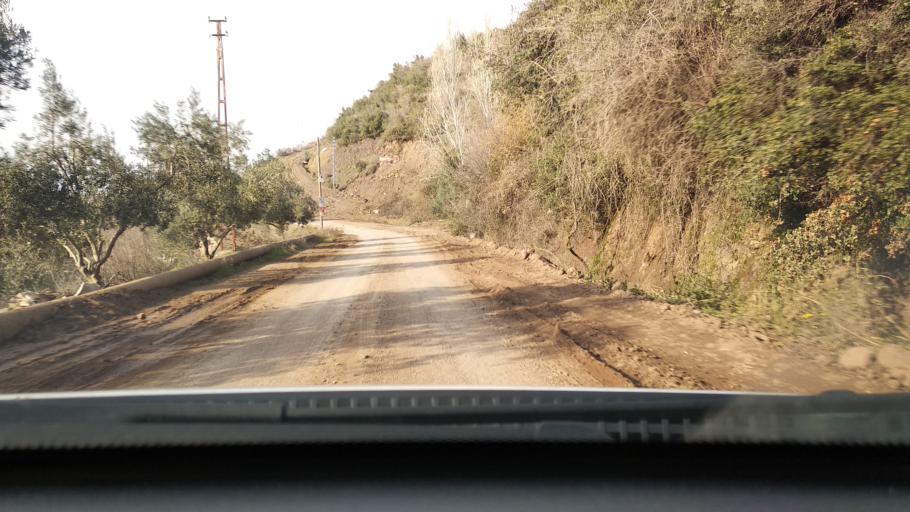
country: TR
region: Mersin
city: Kuzucubelen
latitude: 36.8711
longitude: 34.4684
